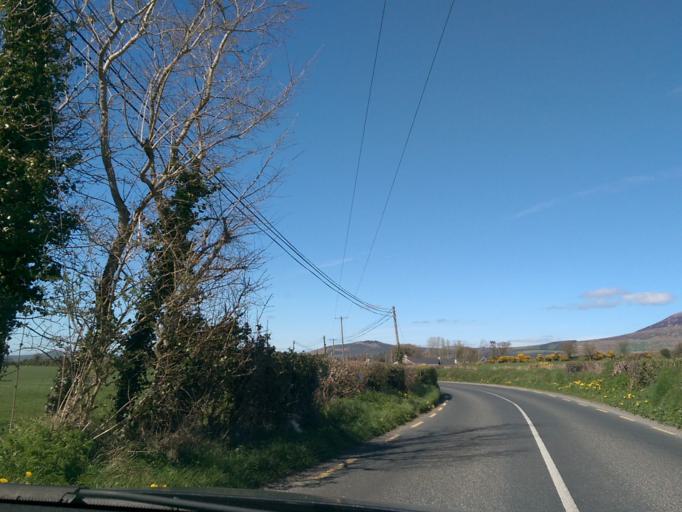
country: IE
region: Leinster
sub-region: Wicklow
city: Baltinglass
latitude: 52.8910
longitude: -6.5954
